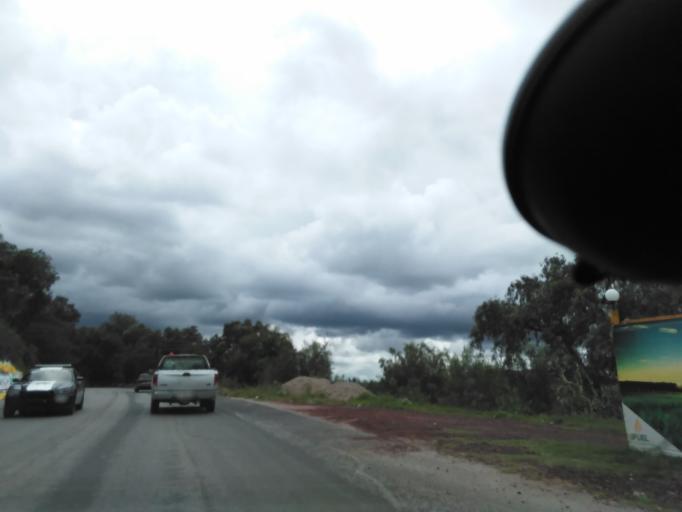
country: MX
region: Hidalgo
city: San Marcos
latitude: 20.0565
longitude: -99.3298
